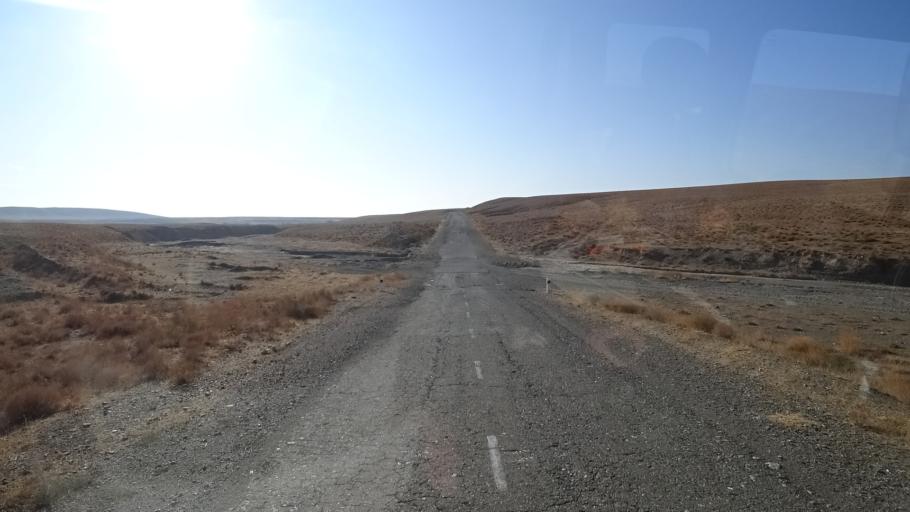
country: UZ
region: Navoiy
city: Beshrabot
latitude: 40.2595
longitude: 65.4794
